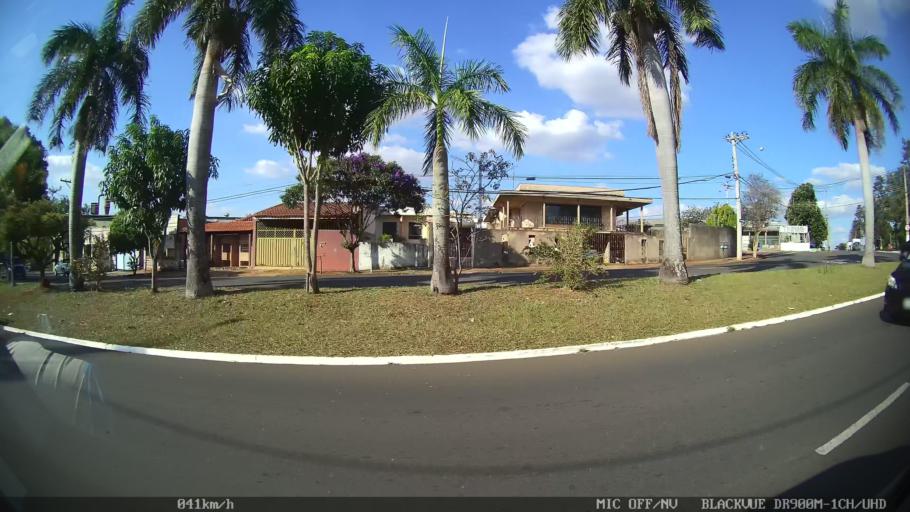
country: BR
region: Sao Paulo
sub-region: Santa Barbara D'Oeste
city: Santa Barbara d'Oeste
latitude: -22.7589
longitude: -47.3980
